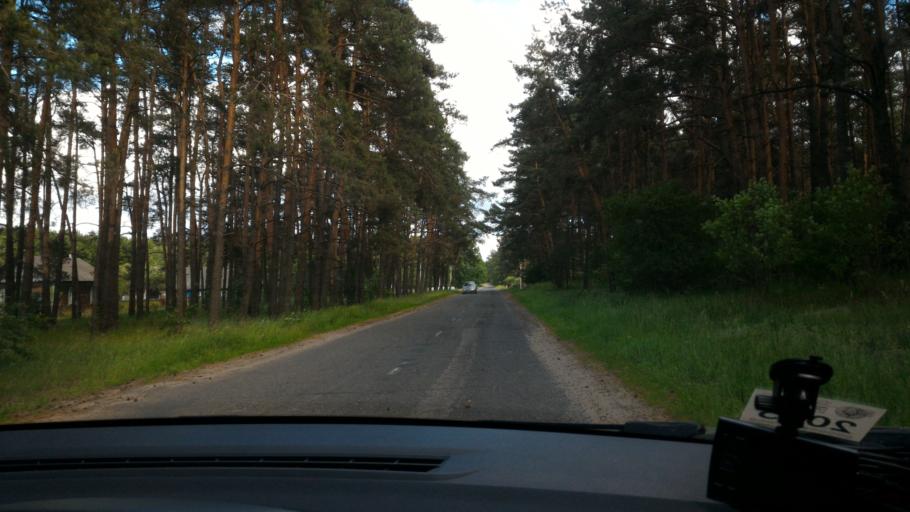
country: BY
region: Brest
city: Ivatsevichy
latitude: 52.7847
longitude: 25.6538
